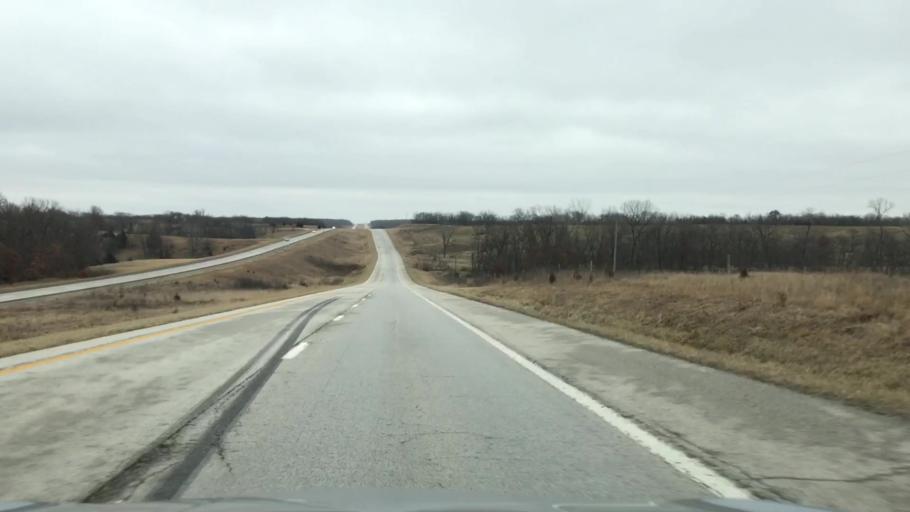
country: US
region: Missouri
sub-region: Linn County
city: Marceline
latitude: 39.7591
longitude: -92.8792
